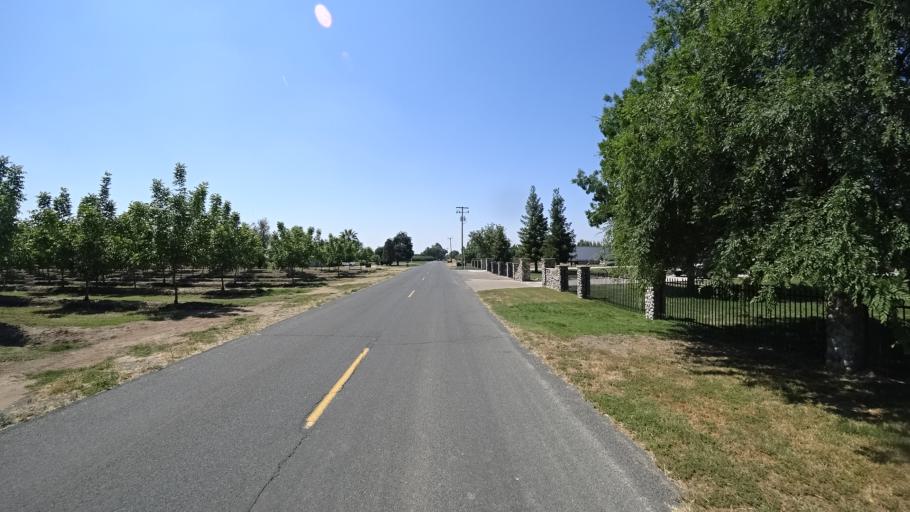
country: US
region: California
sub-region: Fresno County
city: Laton
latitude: 36.4341
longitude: -119.6186
